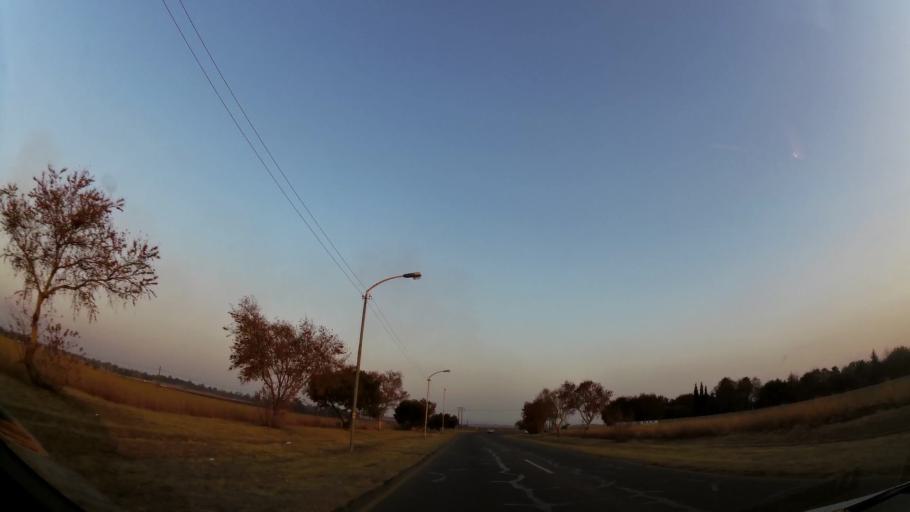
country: ZA
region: Gauteng
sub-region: Ekurhuleni Metropolitan Municipality
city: Springs
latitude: -26.3218
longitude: 28.4492
